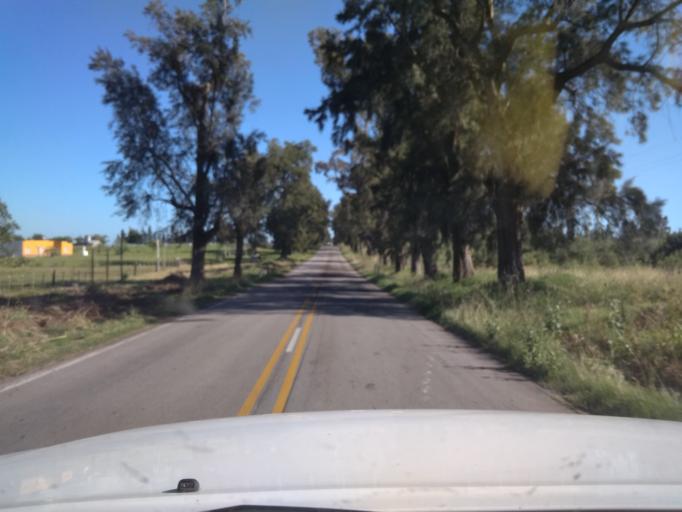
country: UY
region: Canelones
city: San Bautista
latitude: -34.3697
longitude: -55.9595
